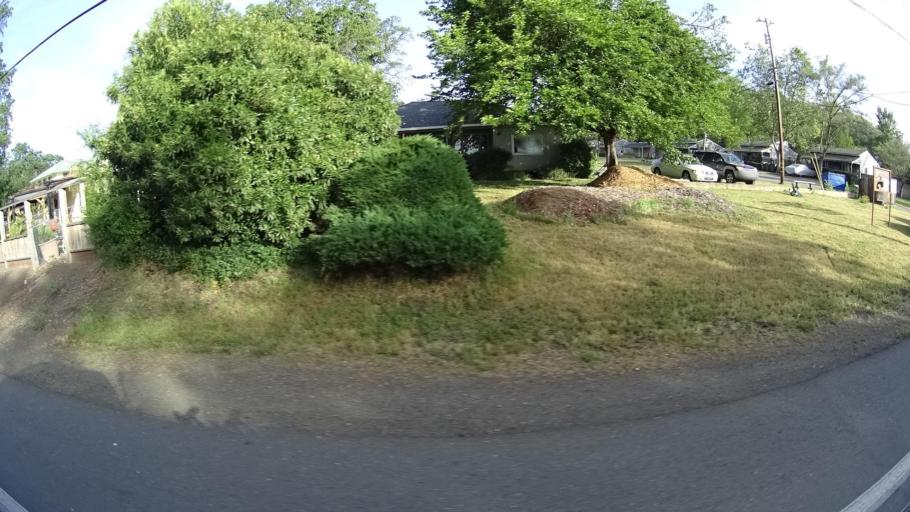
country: US
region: California
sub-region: Lake County
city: North Lakeport
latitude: 39.0804
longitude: -122.9061
